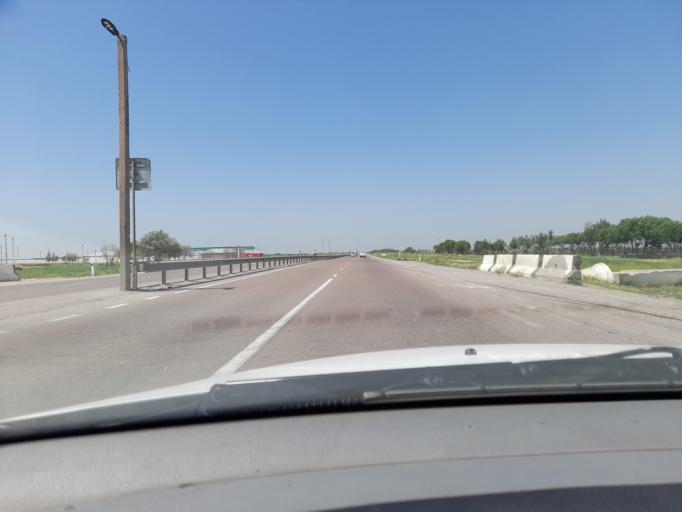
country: KZ
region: Ongtustik Qazaqstan
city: Myrzakent
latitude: 40.5078
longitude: 68.5069
